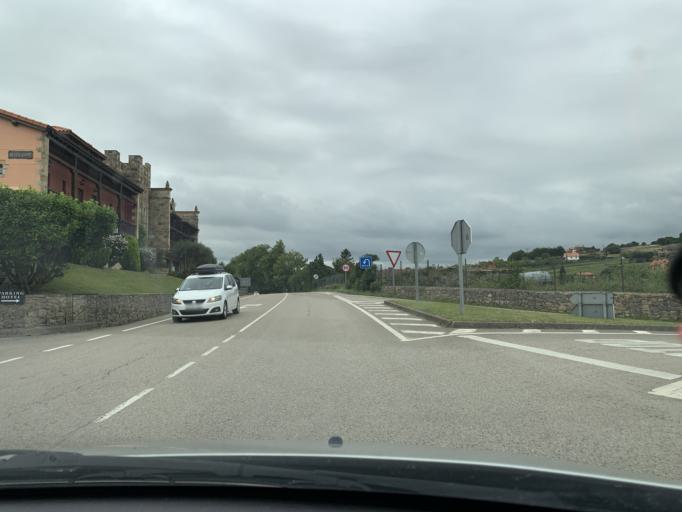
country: ES
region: Cantabria
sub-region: Provincia de Cantabria
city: Santillana
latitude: 43.3855
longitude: -4.1084
